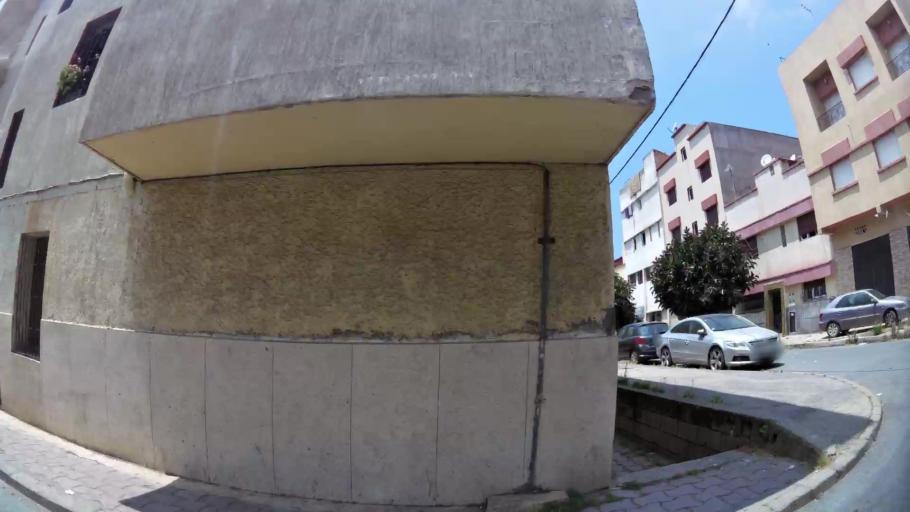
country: MA
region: Rabat-Sale-Zemmour-Zaer
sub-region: Skhirate-Temara
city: Temara
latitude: 33.9786
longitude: -6.8862
